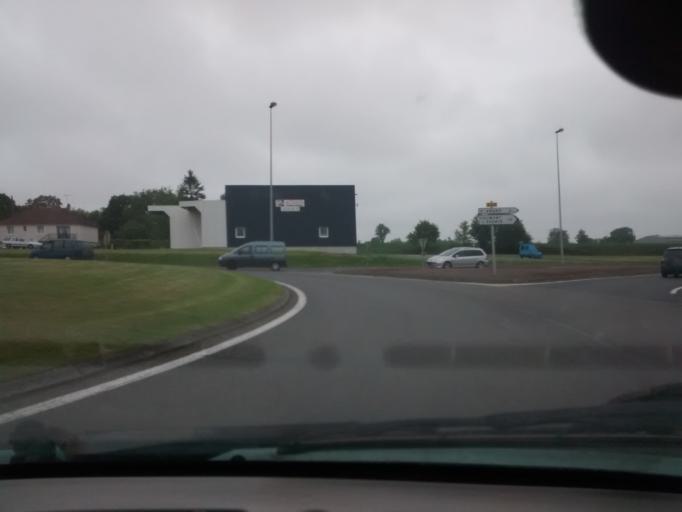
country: FR
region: Lower Normandy
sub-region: Departement de la Manche
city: Torigni-sur-Vire
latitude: 49.0455
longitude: -0.9906
